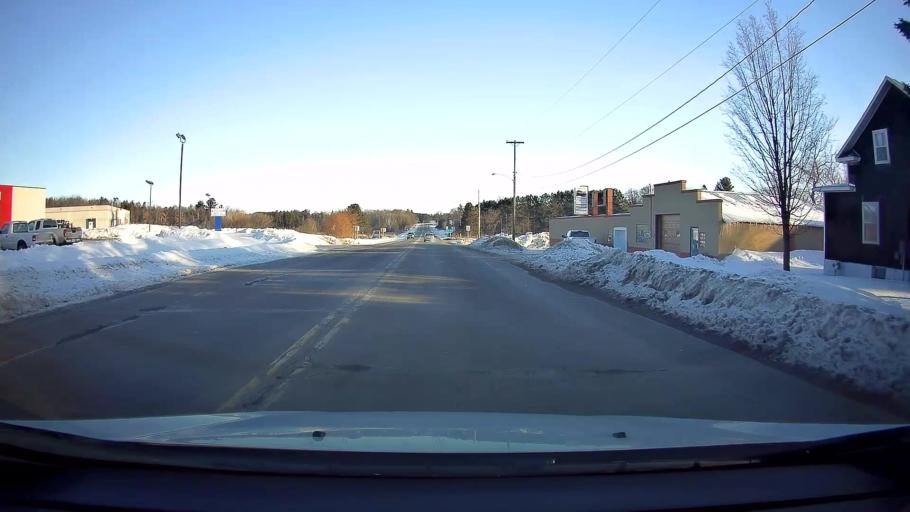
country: US
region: Wisconsin
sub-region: Washburn County
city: Spooner
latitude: 45.8334
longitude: -91.8836
